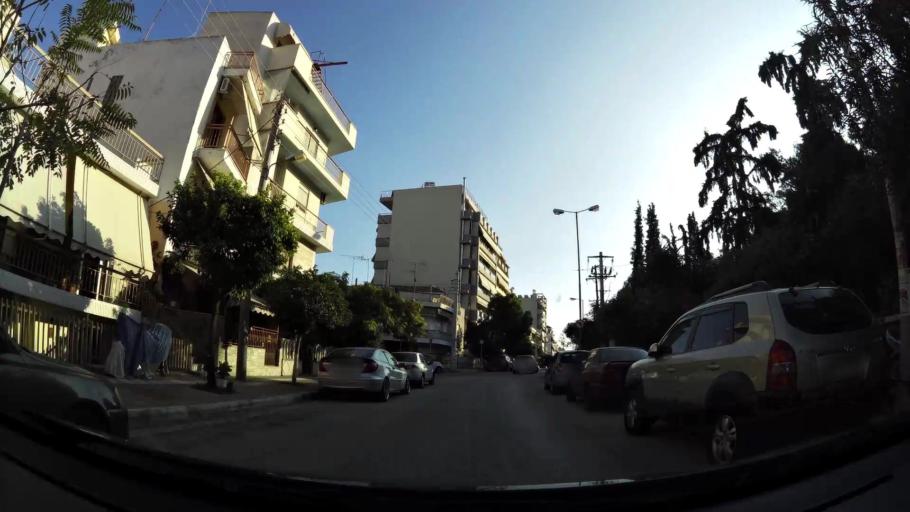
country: GR
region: Attica
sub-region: Nomos Piraios
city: Korydallos
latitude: 37.9742
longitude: 23.6391
